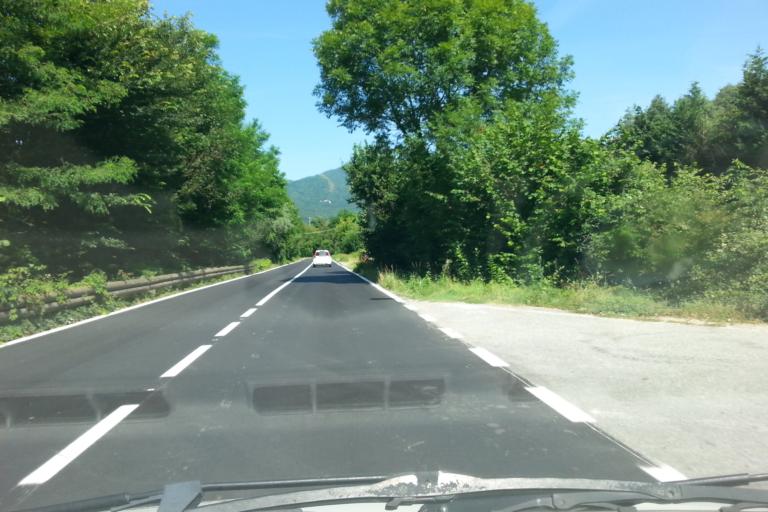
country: IT
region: Piedmont
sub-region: Provincia di Torino
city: Trana
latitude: 45.0513
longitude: 7.3991
